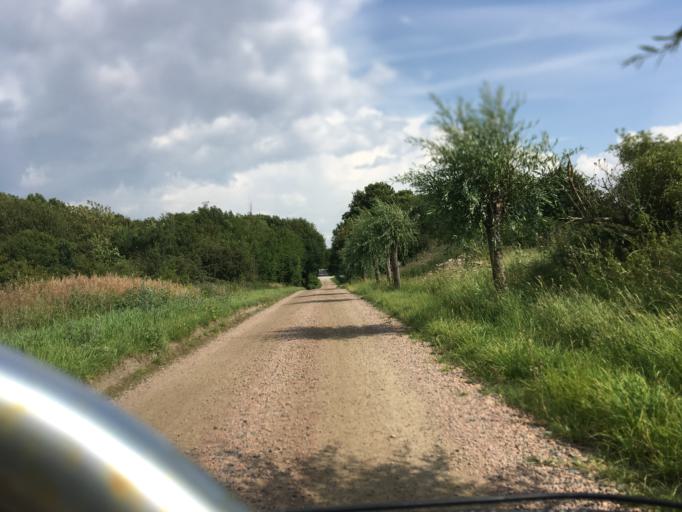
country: SE
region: Skane
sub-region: Lunds Kommun
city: Lund
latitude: 55.6974
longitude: 13.1599
